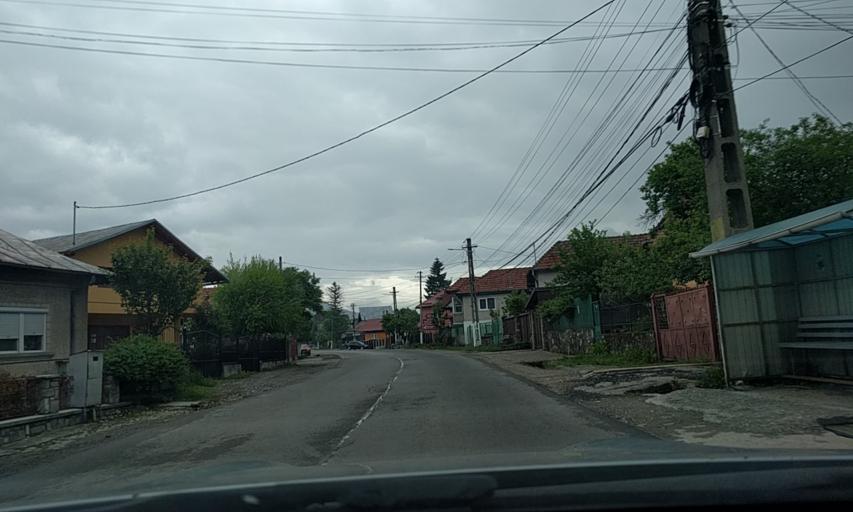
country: RO
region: Dambovita
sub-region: Comuna Moroeni
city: Moroeni
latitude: 45.2254
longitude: 25.4308
